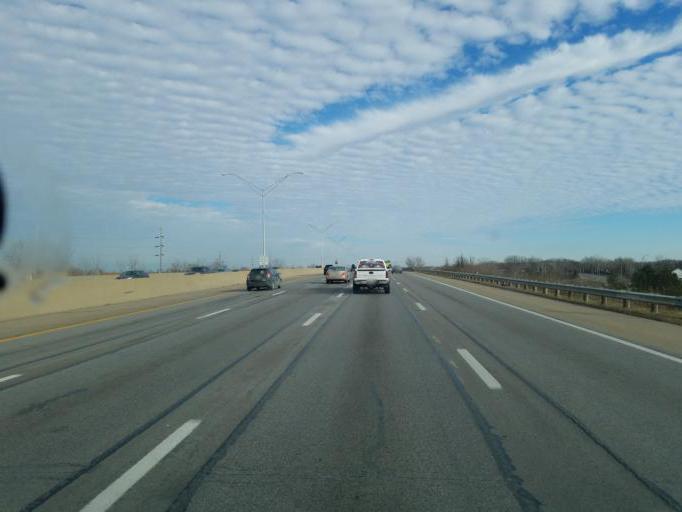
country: US
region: Ohio
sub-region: Franklin County
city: Bexley
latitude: 39.9798
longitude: -82.9653
